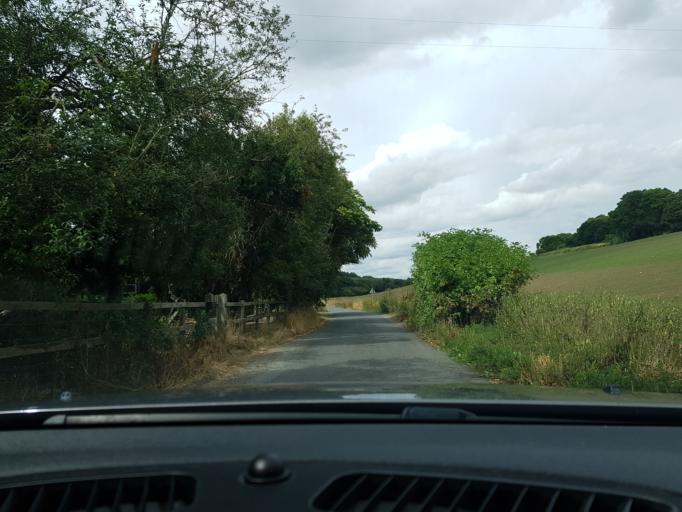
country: GB
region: England
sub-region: West Berkshire
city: Kintbury
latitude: 51.4252
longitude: -1.4728
